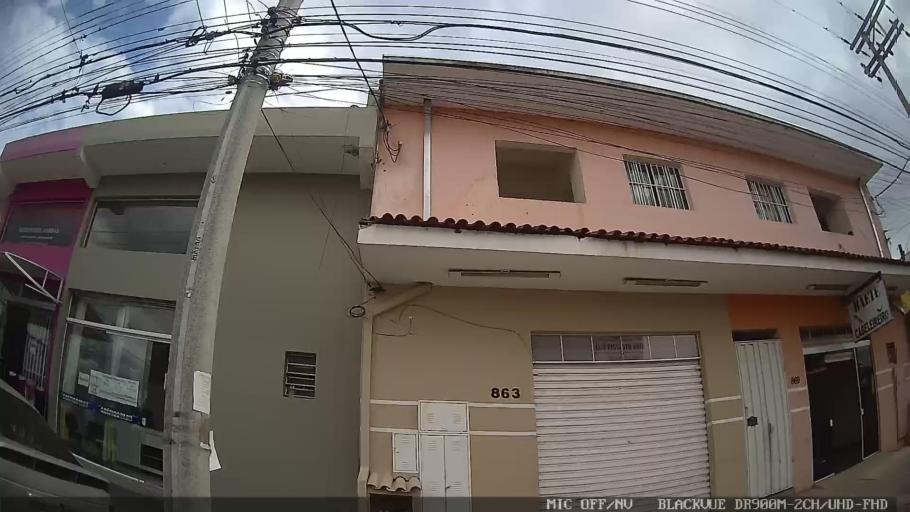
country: BR
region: Sao Paulo
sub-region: Indaiatuba
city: Indaiatuba
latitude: -23.1266
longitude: -47.2385
